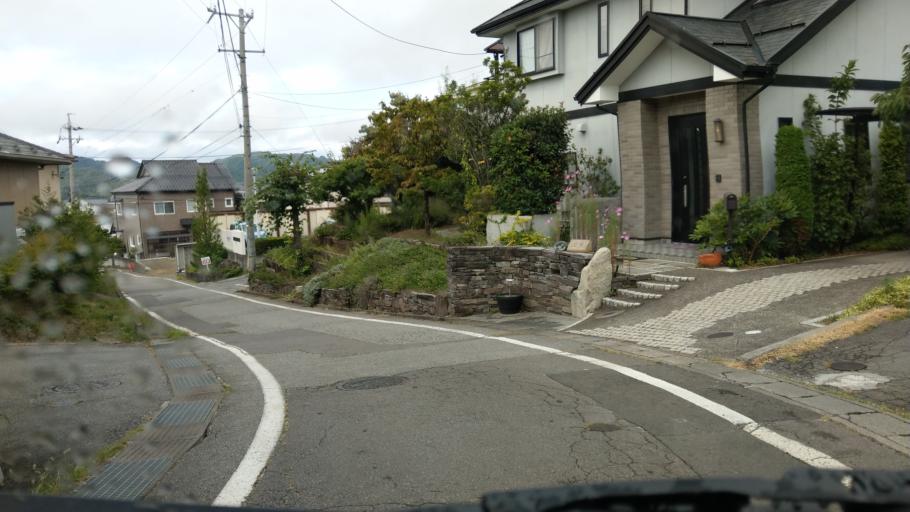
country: JP
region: Nagano
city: Komoro
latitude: 36.3336
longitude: 138.4236
